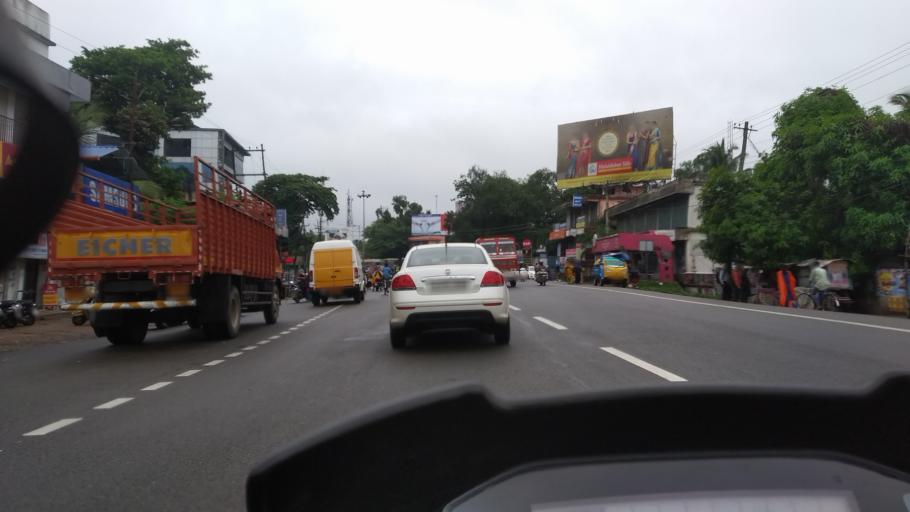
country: IN
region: Kerala
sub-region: Alappuzha
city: Mavelikara
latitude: 9.2781
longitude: 76.4597
